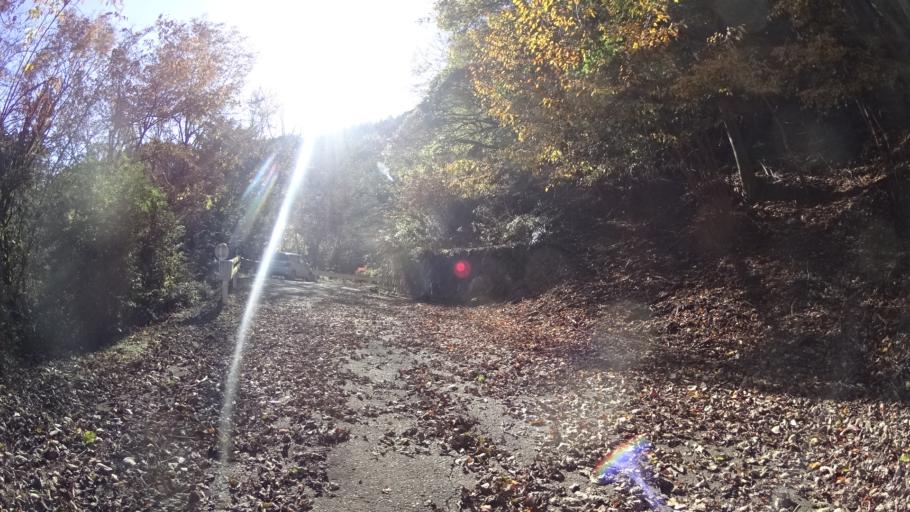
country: JP
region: Kanagawa
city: Atsugi
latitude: 35.5086
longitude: 139.2677
